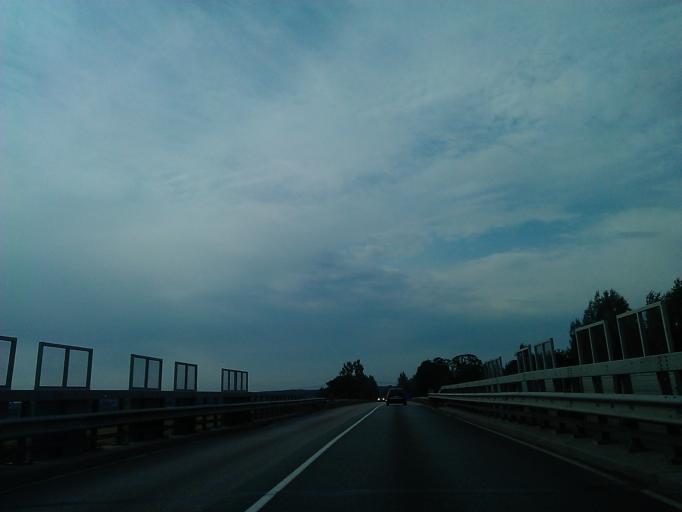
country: LV
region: Salaspils
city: Salaspils
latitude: 56.8530
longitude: 24.4001
